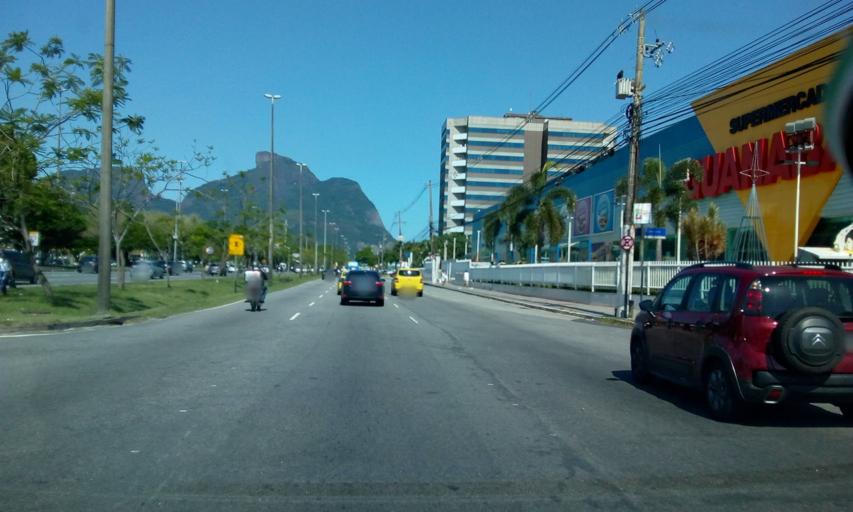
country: BR
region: Rio de Janeiro
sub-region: Rio De Janeiro
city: Rio de Janeiro
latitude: -23.0006
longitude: -43.3390
